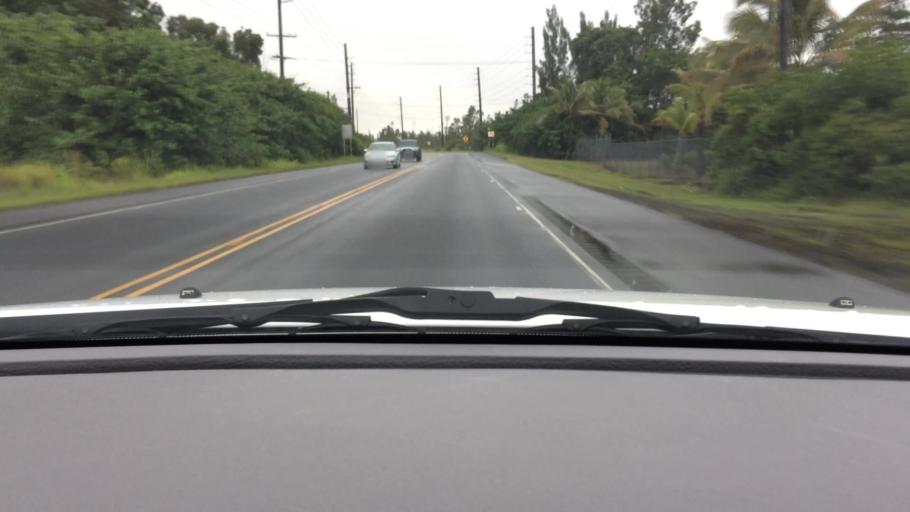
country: US
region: Hawaii
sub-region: Hawaii County
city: Ainaloa
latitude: 19.5399
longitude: -154.9733
